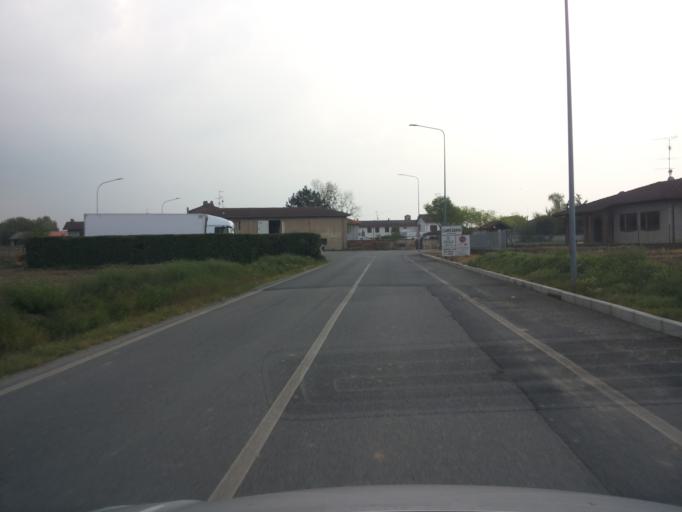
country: IT
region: Piedmont
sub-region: Provincia di Vercelli
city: Caresana
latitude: 45.2235
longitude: 8.4983
